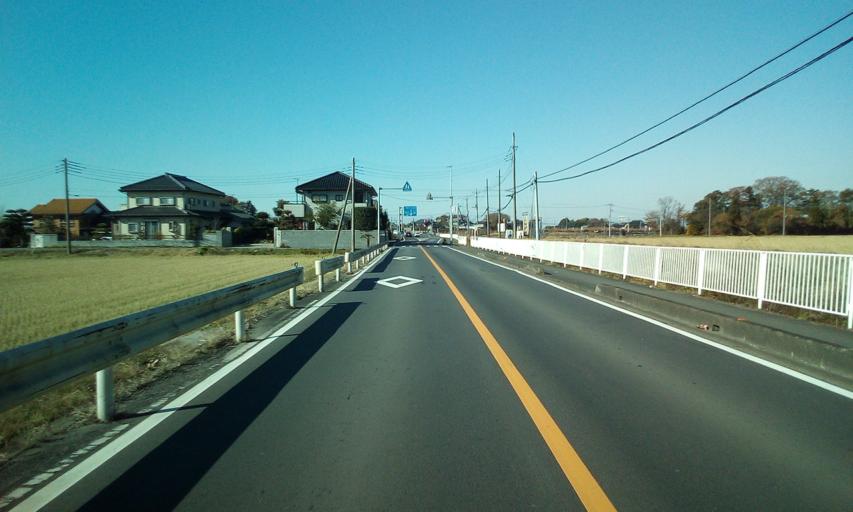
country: JP
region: Saitama
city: Sugito
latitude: 36.0519
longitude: 139.7748
